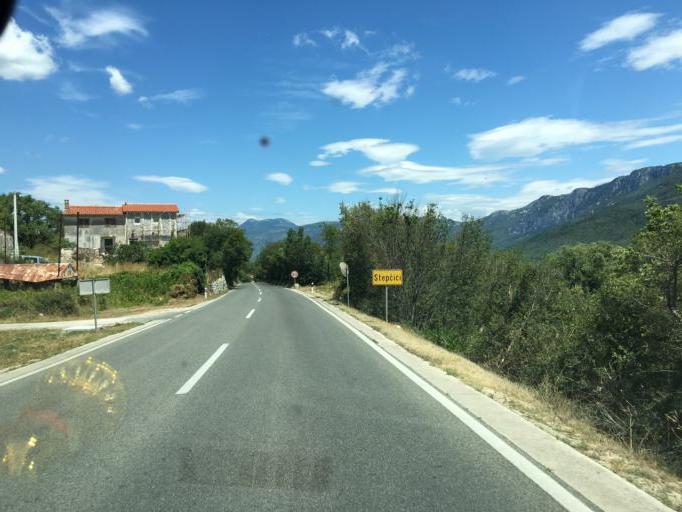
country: HR
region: Istarska
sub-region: Grad Labin
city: Labin
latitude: 45.1410
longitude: 14.1477
